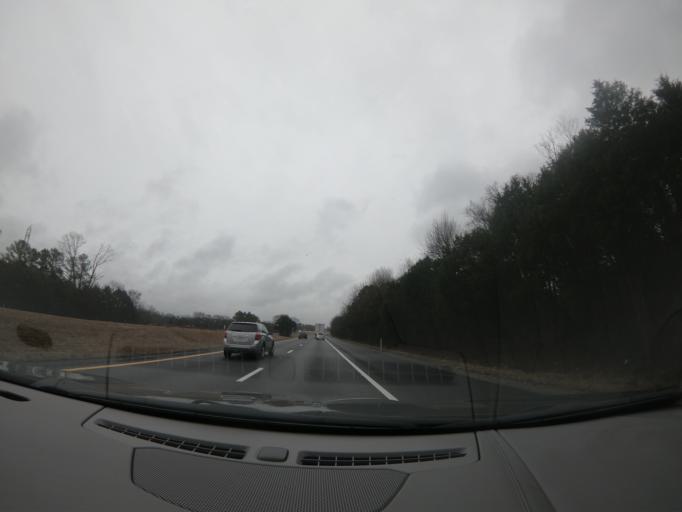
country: US
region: Tennessee
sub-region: Rutherford County
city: Plainview
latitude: 35.7543
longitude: -86.3467
